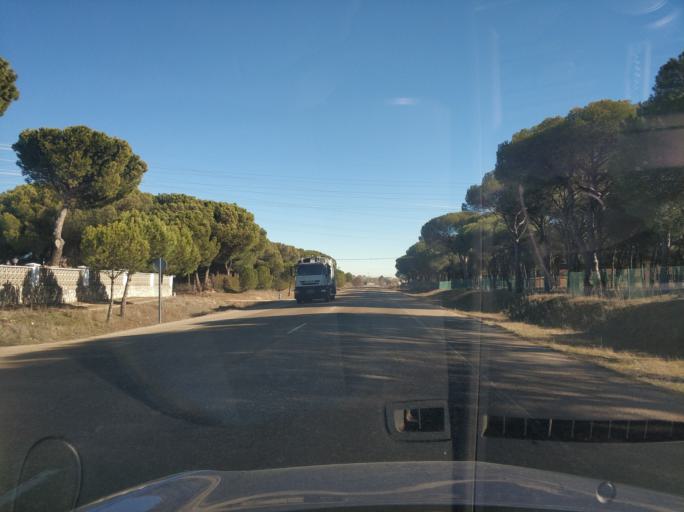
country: ES
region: Castille and Leon
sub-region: Provincia de Valladolid
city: Tordesillas
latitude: 41.4932
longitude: -5.0111
